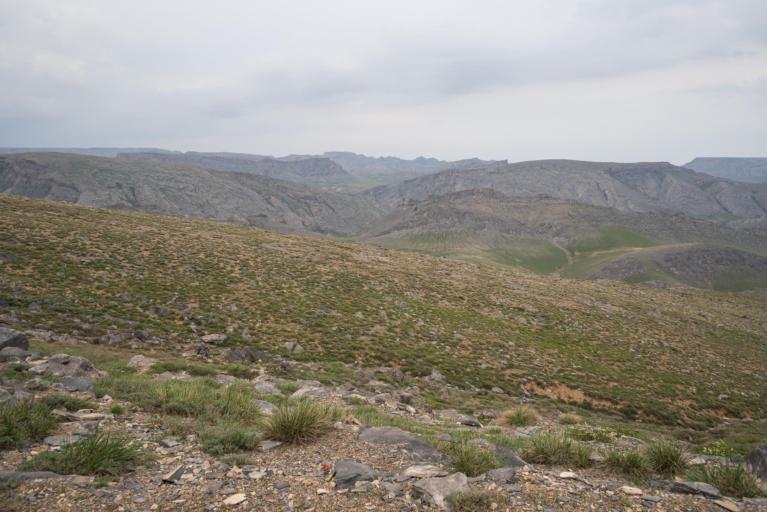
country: KZ
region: Ongtustik Qazaqstan
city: Ashchysay
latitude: 43.5656
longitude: 68.8732
